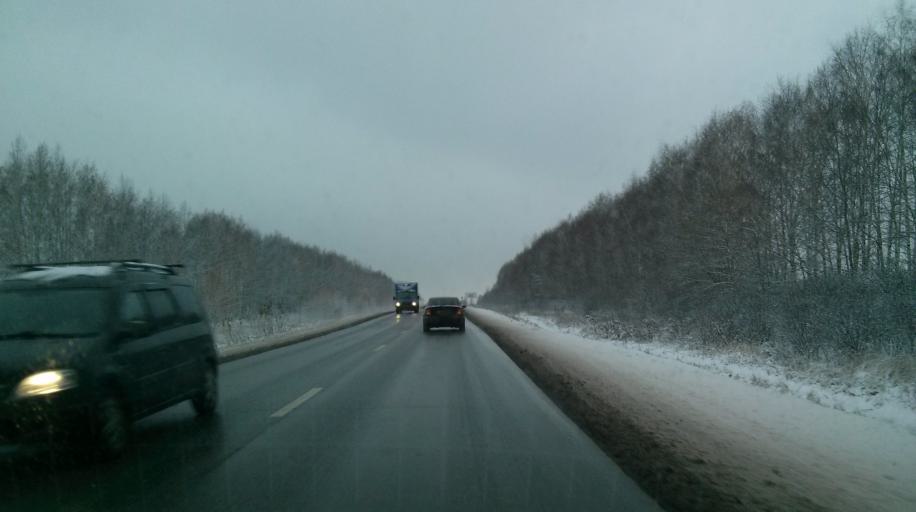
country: RU
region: Nizjnij Novgorod
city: Bogorodsk
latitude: 56.0872
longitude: 43.5429
